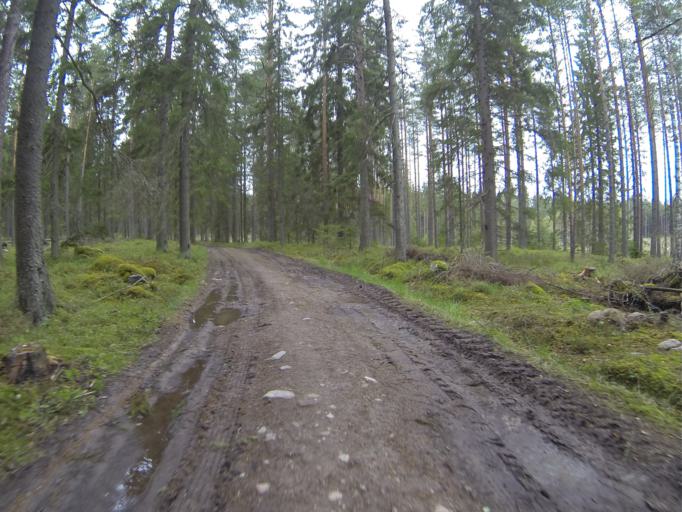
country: FI
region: Varsinais-Suomi
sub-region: Salo
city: Pertteli
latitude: 60.4007
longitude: 23.2040
